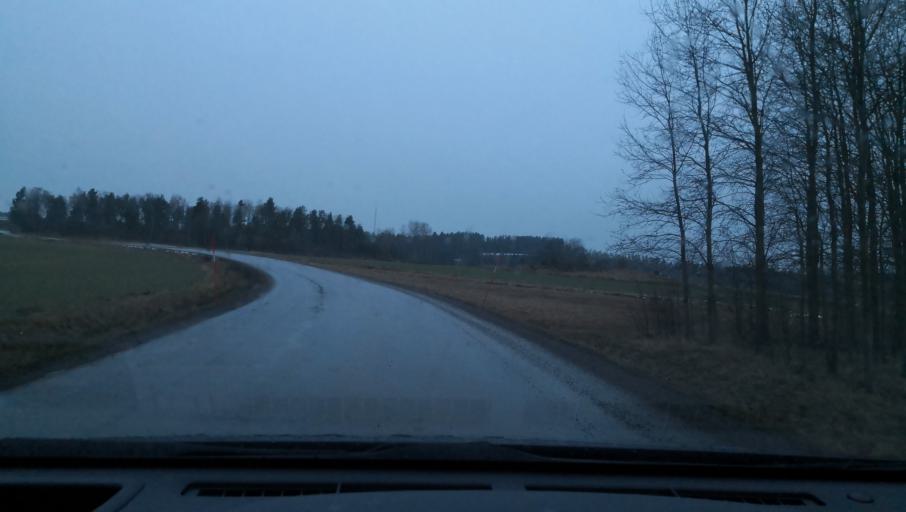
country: SE
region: Soedermanland
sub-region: Eskilstuna Kommun
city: Arla
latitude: 59.4047
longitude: 16.6815
